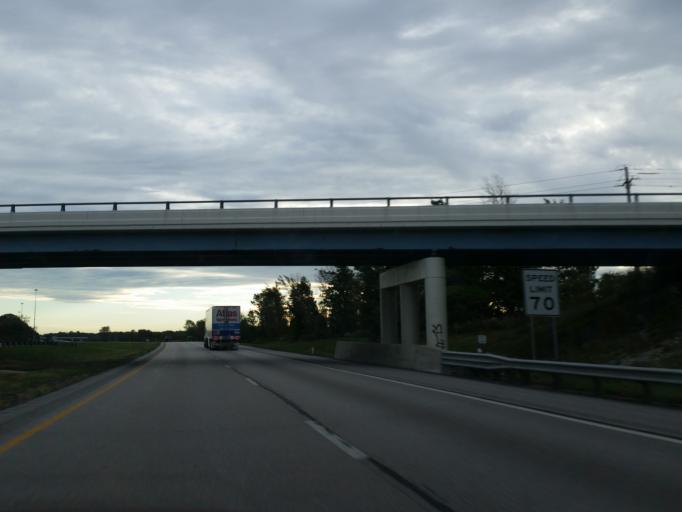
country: US
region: Ohio
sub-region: Ashtabula County
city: Conneaut
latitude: 41.9202
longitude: -80.5557
